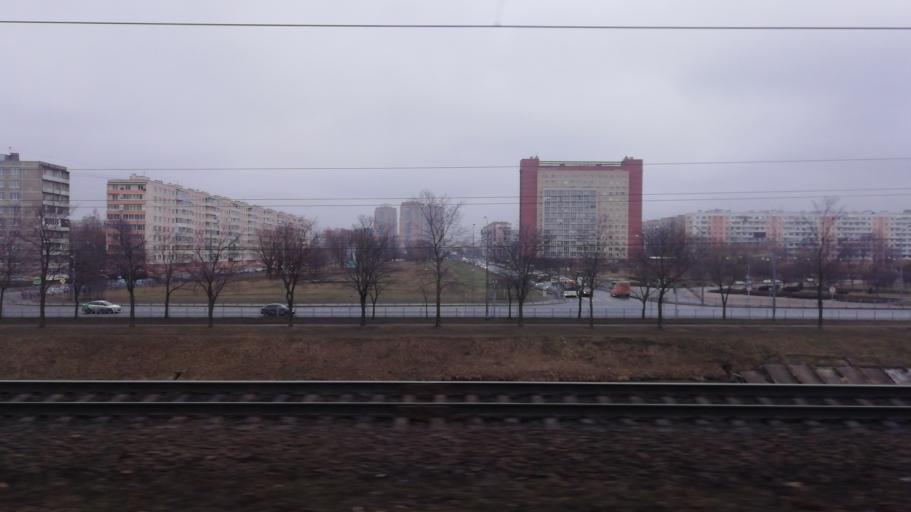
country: RU
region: St.-Petersburg
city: Kupchino
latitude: 59.8662
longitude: 30.3583
